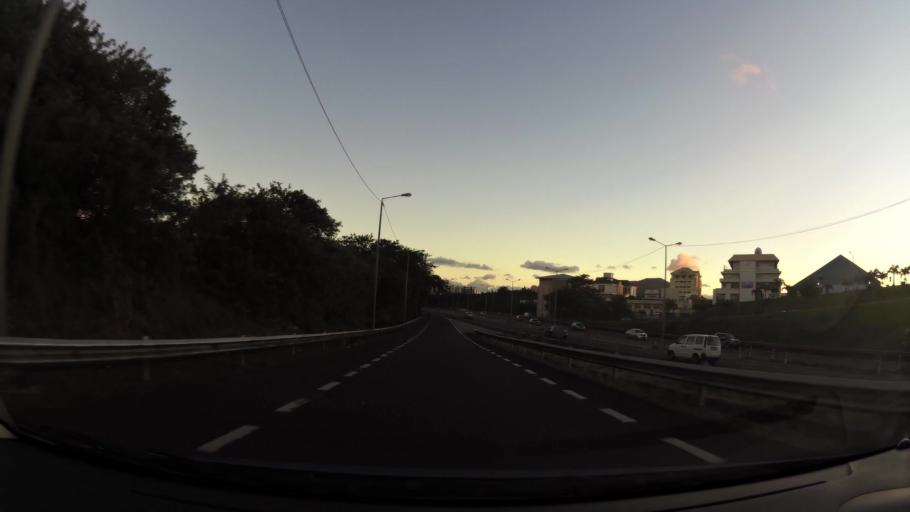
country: MU
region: Moka
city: Moka
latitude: -20.2329
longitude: 57.5008
